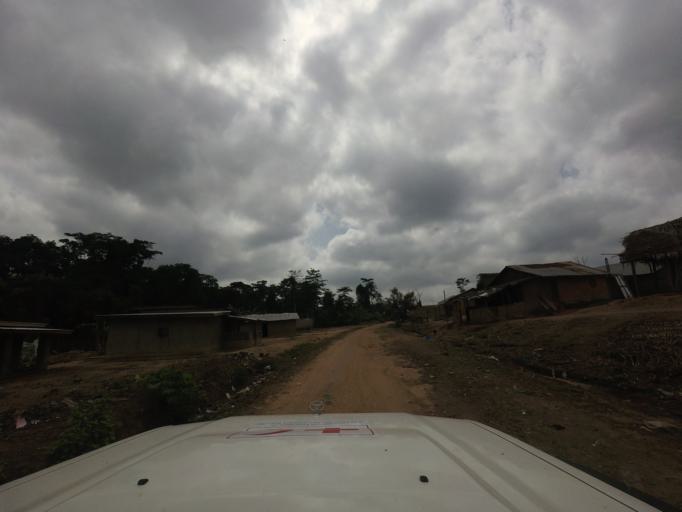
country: LR
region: Lofa
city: Voinjama
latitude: 8.4100
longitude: -9.7172
